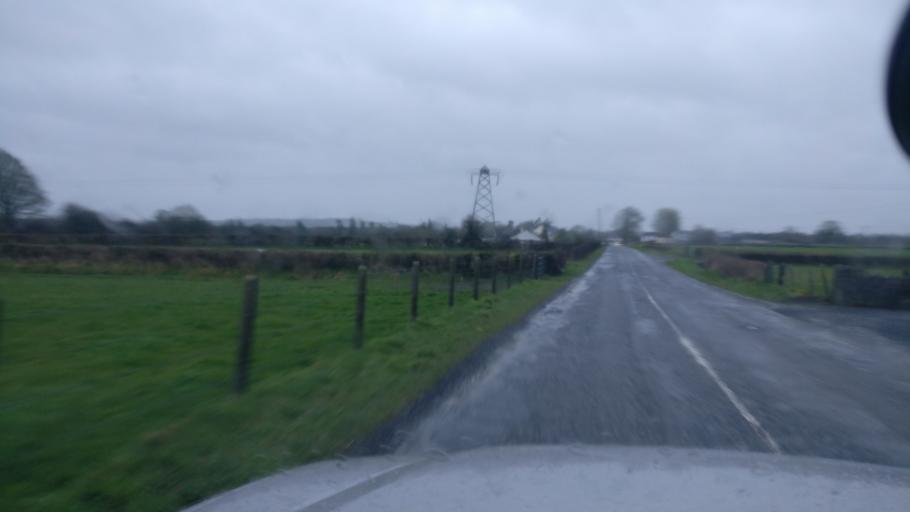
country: IE
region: Connaught
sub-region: County Galway
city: Ballinasloe
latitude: 53.2496
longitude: -8.1766
